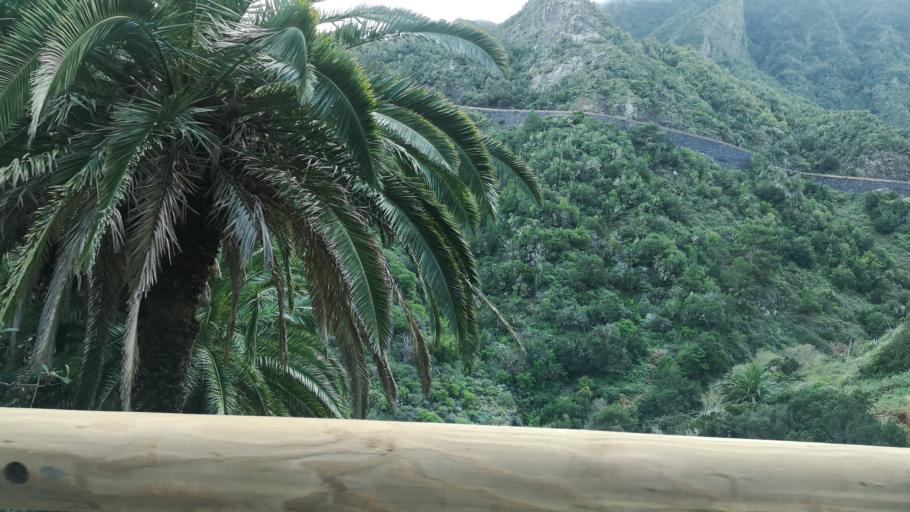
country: ES
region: Canary Islands
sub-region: Provincia de Santa Cruz de Tenerife
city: Hermigua
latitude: 28.1384
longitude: -17.2010
